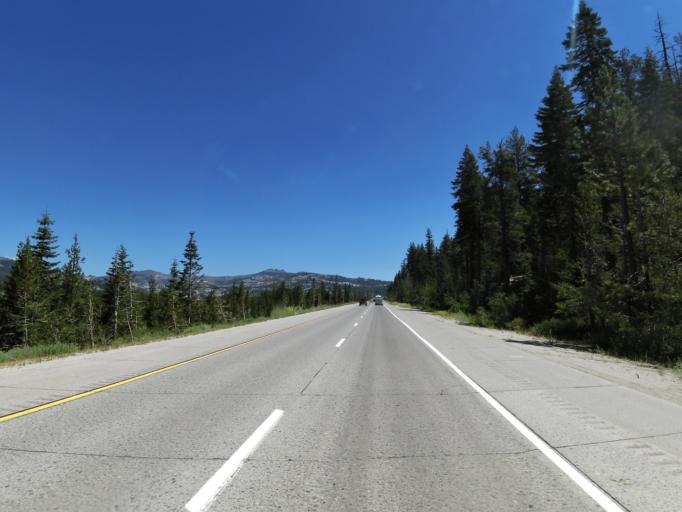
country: US
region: California
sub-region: Nevada County
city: Truckee
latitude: 39.3202
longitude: -120.4246
